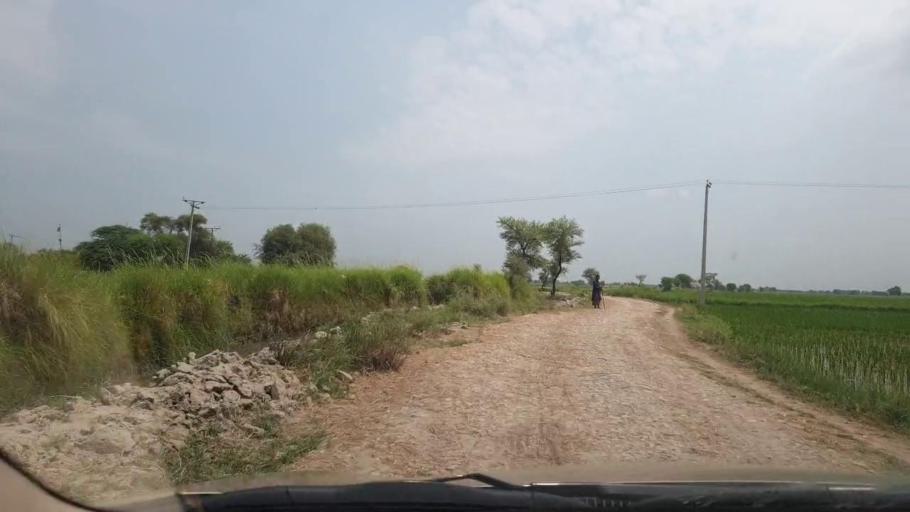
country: PK
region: Sindh
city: Goth Garelo
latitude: 27.5214
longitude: 68.1214
